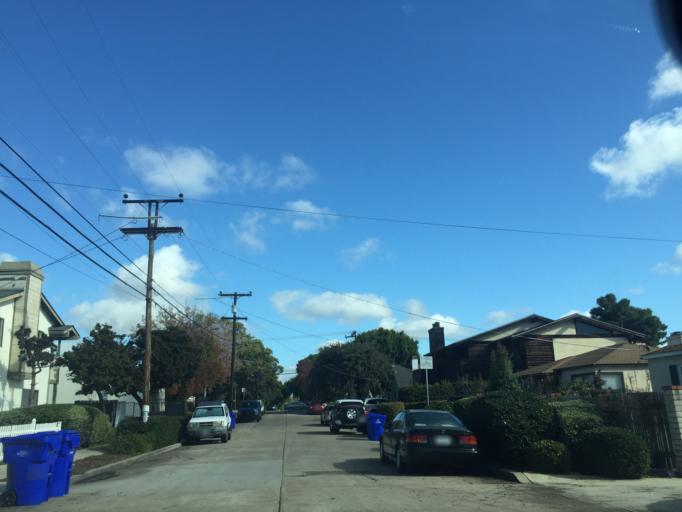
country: US
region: California
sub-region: San Diego County
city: La Jolla
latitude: 32.7952
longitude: -117.2385
